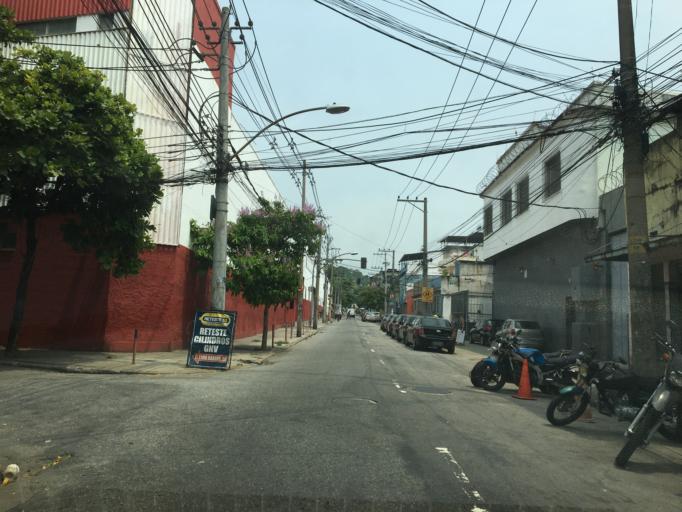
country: BR
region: Rio de Janeiro
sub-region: Rio De Janeiro
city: Rio de Janeiro
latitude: -22.8884
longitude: -43.2263
